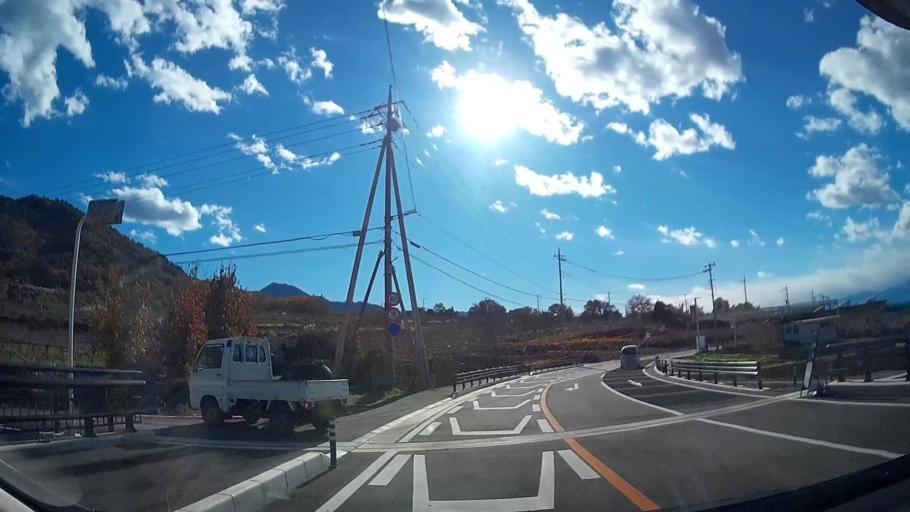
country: JP
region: Yamanashi
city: Enzan
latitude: 35.6380
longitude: 138.7078
